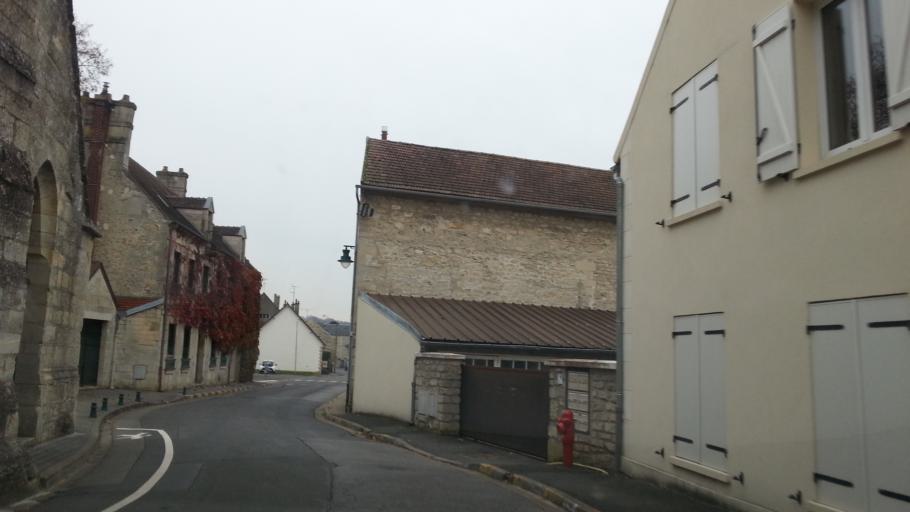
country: FR
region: Picardie
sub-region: Departement de l'Oise
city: Villers-sous-Saint-Leu
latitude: 49.2133
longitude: 2.3982
